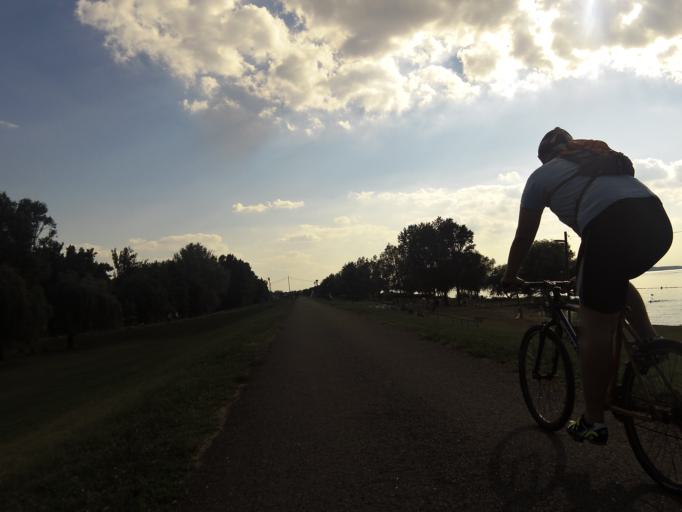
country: HU
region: Jasz-Nagykun-Szolnok
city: Abadszalok
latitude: 47.4828
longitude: 20.5876
